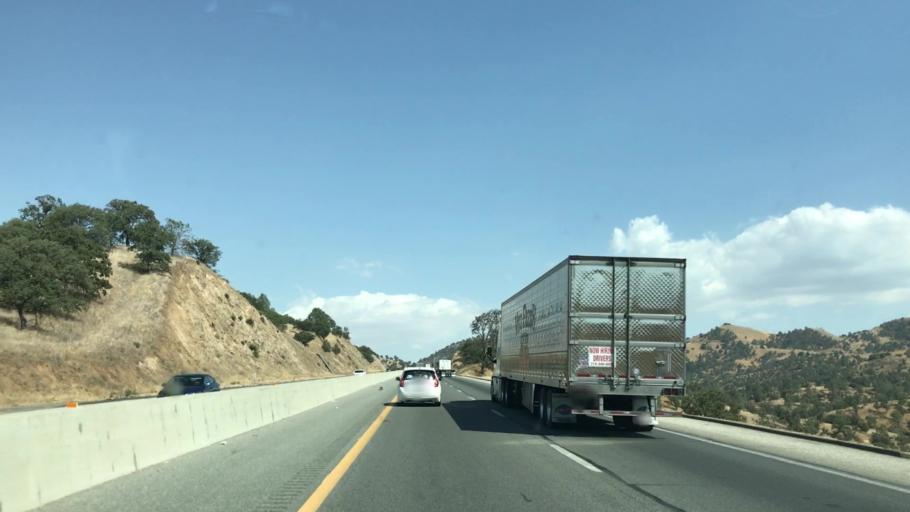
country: US
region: California
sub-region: Kern County
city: Golden Hills
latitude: 35.1977
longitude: -118.5177
